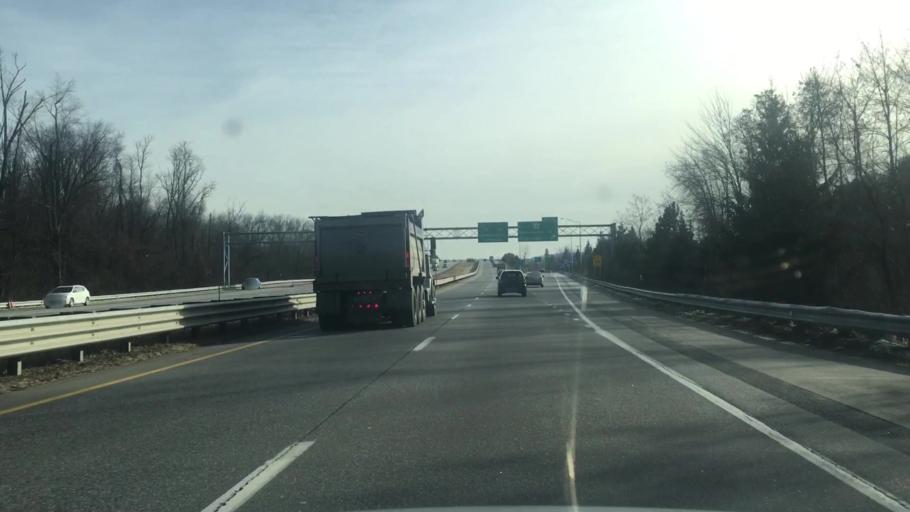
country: US
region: New Hampshire
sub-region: Merrimack County
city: Concord
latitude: 43.1991
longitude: -71.5290
